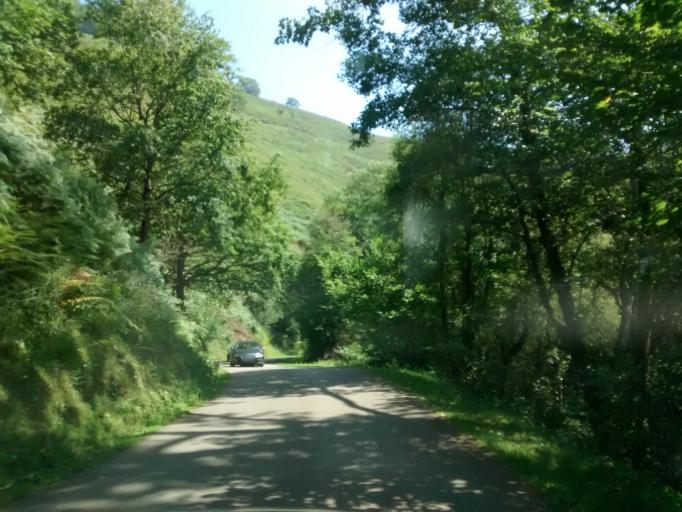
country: ES
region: Cantabria
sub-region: Provincia de Cantabria
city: Ruente
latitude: 43.2409
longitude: -4.2335
